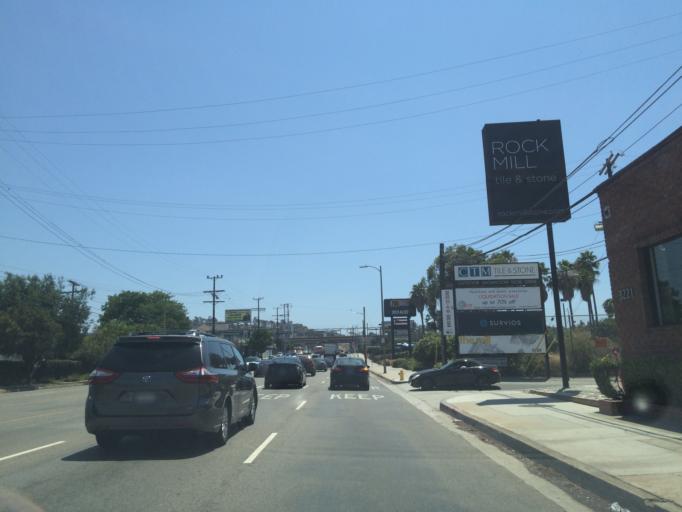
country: US
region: California
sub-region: Los Angeles County
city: Culver City
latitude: 34.0293
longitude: -118.3721
